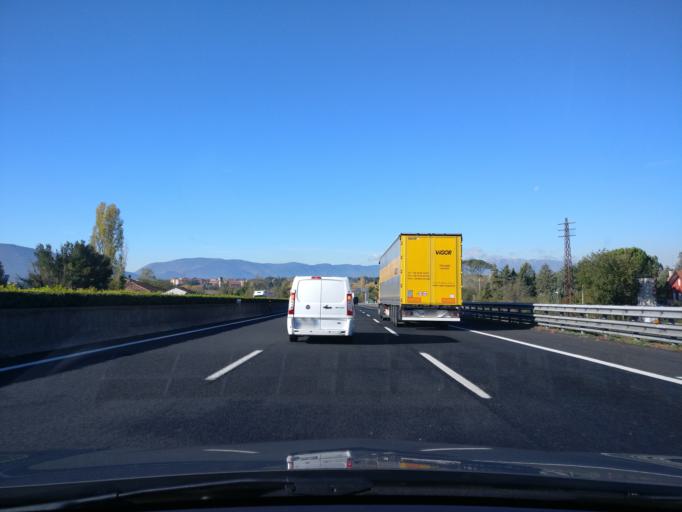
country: IT
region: Latium
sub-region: Provincia di Frosinone
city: Ceprano
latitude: 41.5434
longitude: 13.5270
